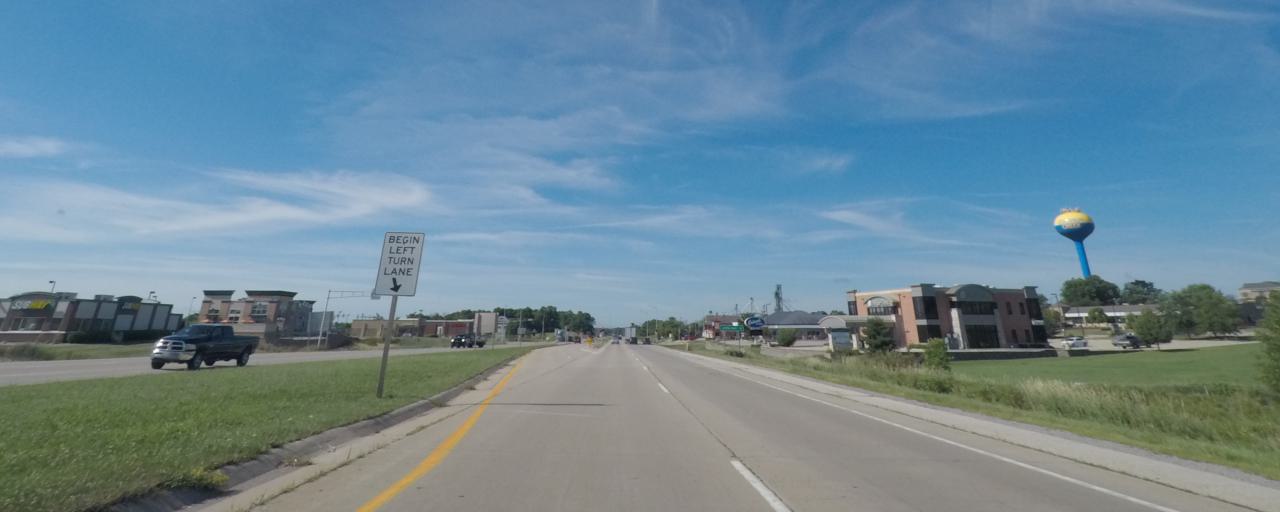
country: US
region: Wisconsin
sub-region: Jefferson County
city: Johnson Creek
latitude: 43.0846
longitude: -88.7623
